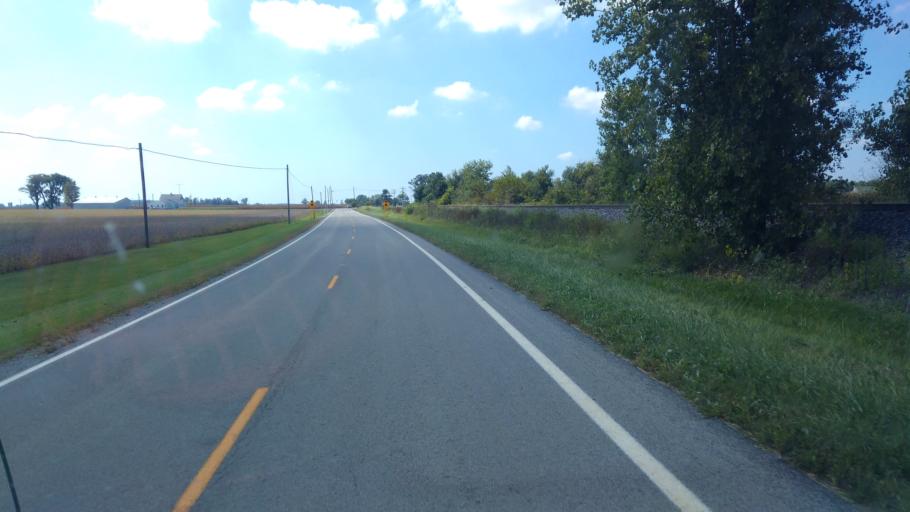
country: US
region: Ohio
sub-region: Hardin County
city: Ada
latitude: 40.7768
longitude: -83.7611
